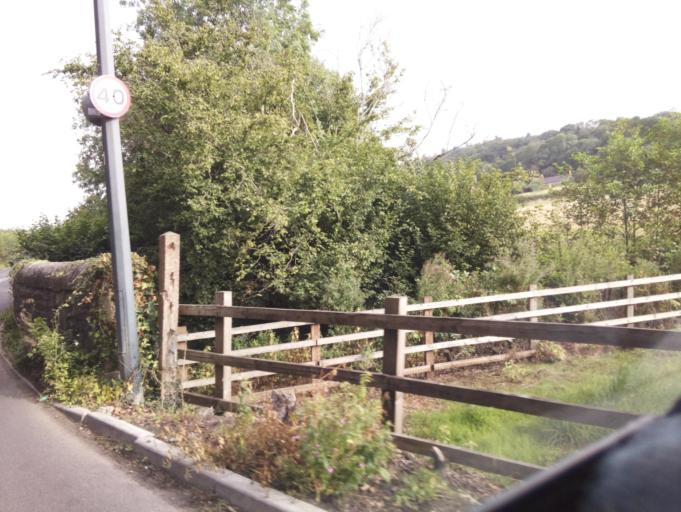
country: GB
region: England
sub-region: North Somerset
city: Long Ashton
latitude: 51.4259
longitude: -2.7000
